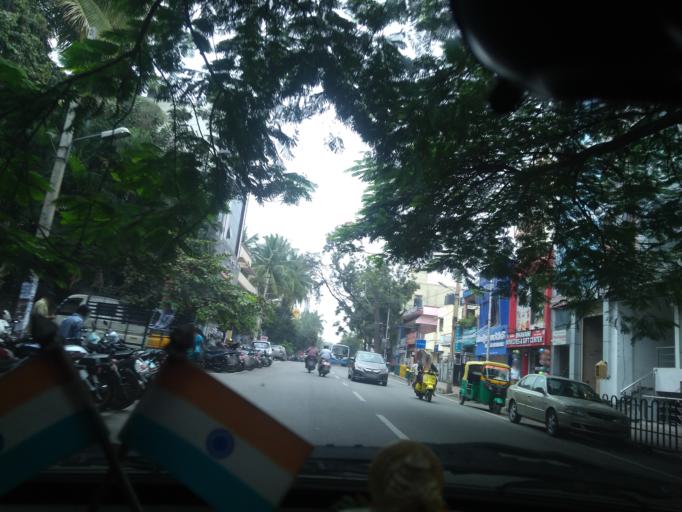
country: IN
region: Karnataka
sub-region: Bangalore Urban
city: Bangalore
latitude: 13.0004
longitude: 77.5505
